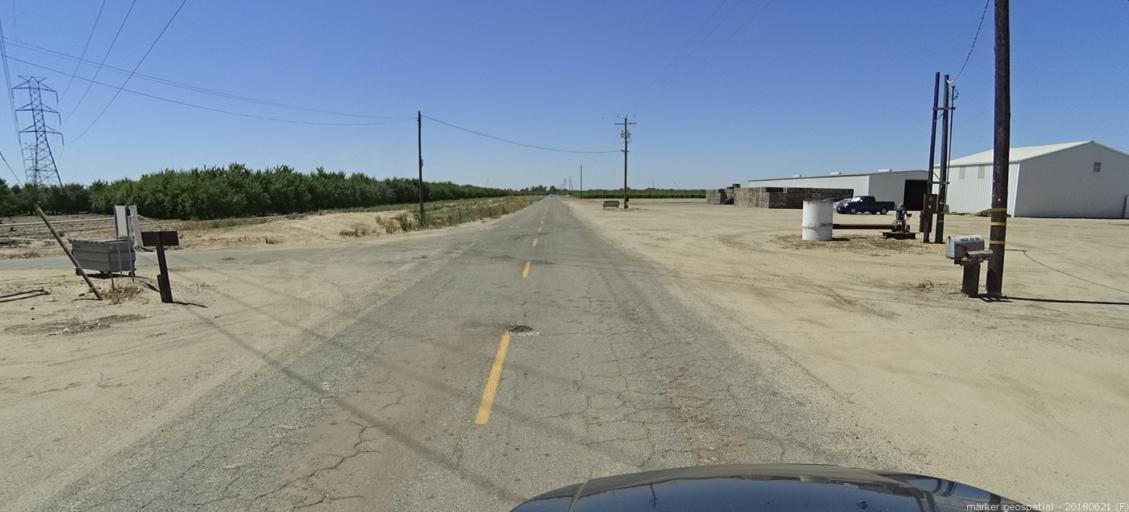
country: US
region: California
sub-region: Fresno County
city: Biola
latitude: 36.8586
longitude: -119.9293
